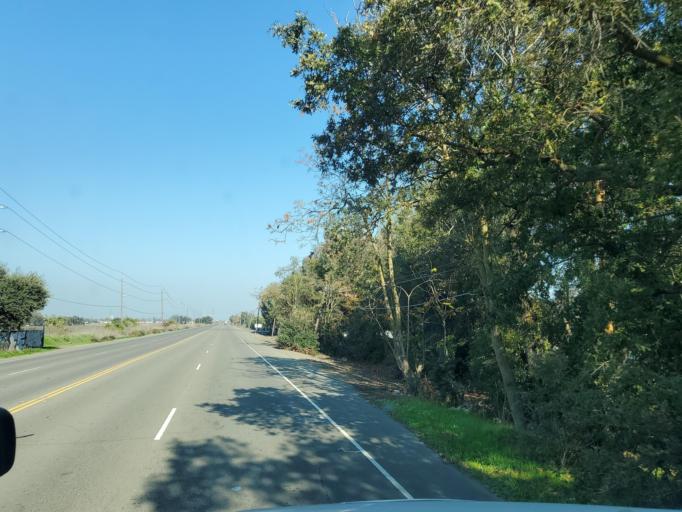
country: US
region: California
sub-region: San Joaquin County
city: French Camp
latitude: 37.8983
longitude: -121.2757
